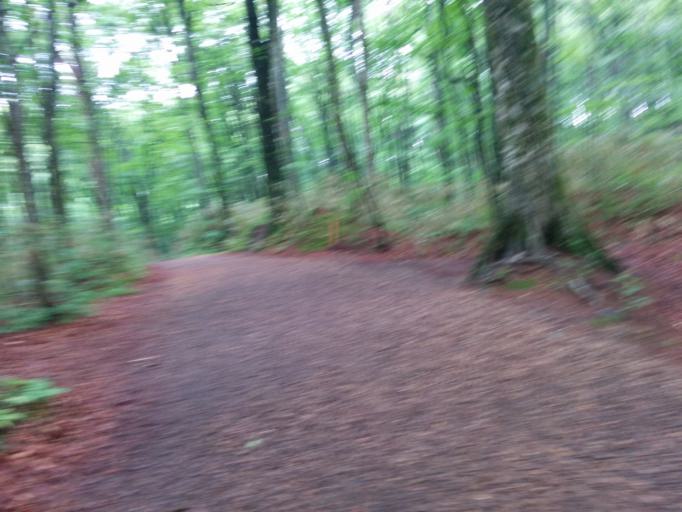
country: JP
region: Akita
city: Noshiromachi
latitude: 40.5610
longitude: 139.9834
